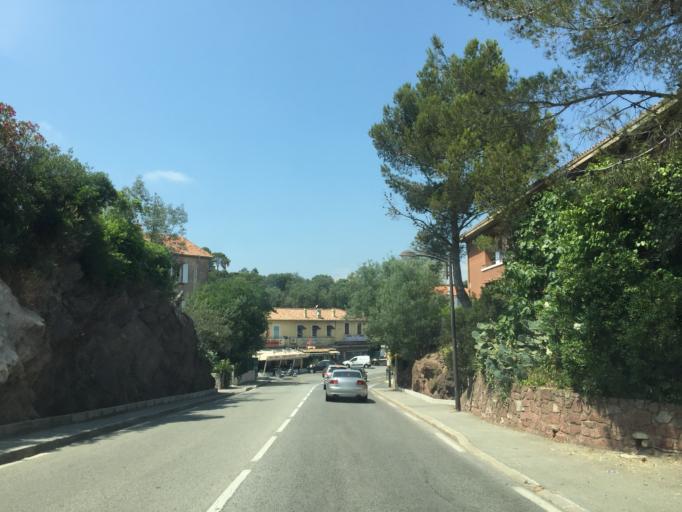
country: FR
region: Provence-Alpes-Cote d'Azur
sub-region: Departement du Var
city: Saint-Raphael
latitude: 43.4284
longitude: 6.8569
